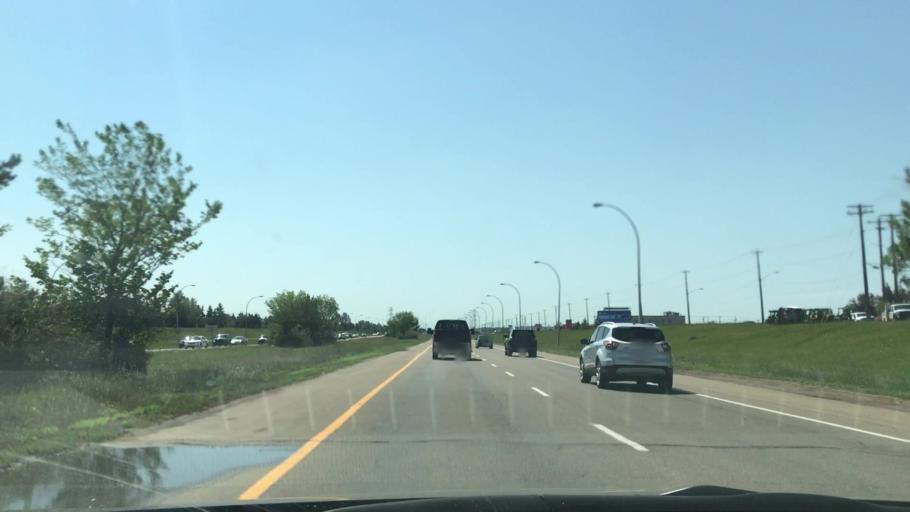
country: CA
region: Alberta
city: Edmonton
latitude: 53.4728
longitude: -113.4667
